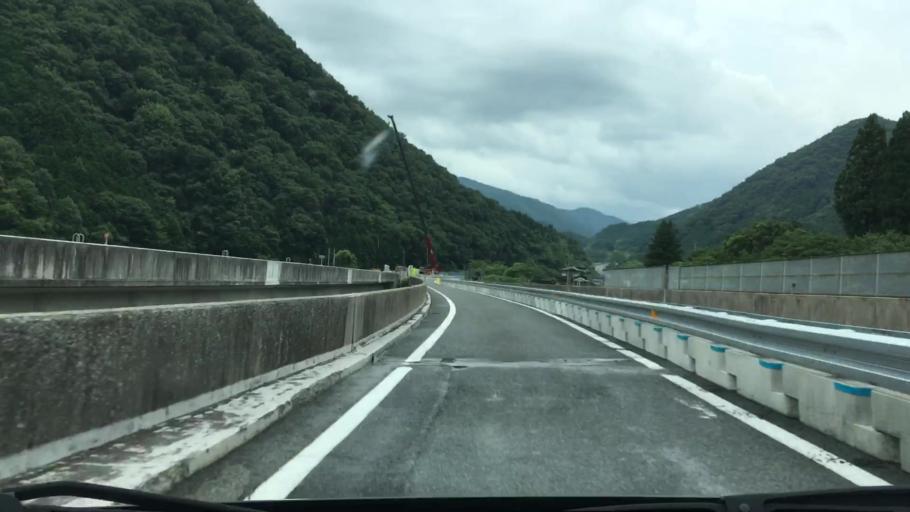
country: JP
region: Okayama
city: Niimi
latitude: 35.0069
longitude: 133.4063
